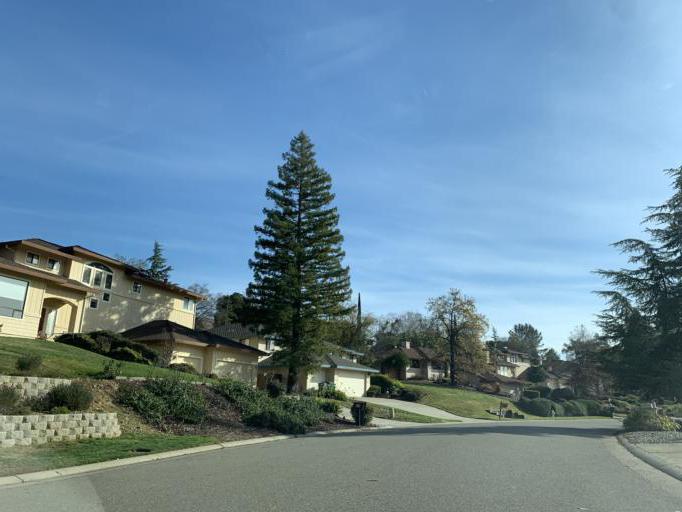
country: US
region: California
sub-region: El Dorado County
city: El Dorado Hills
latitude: 38.6552
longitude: -121.0776
